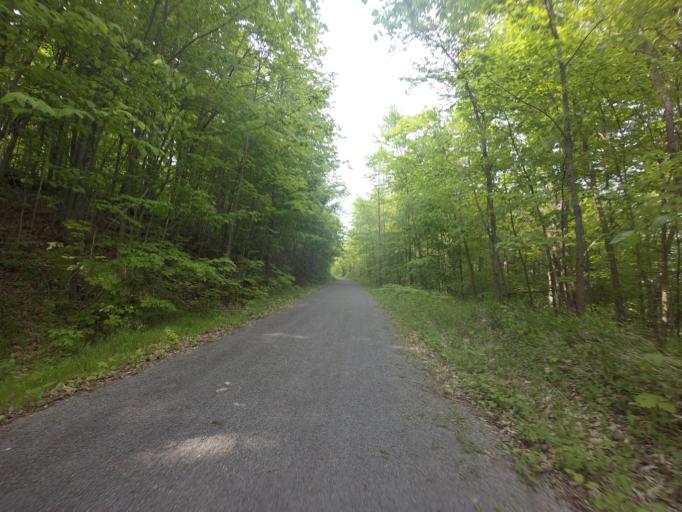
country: CA
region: Ontario
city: Kingston
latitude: 44.3947
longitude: -76.6408
